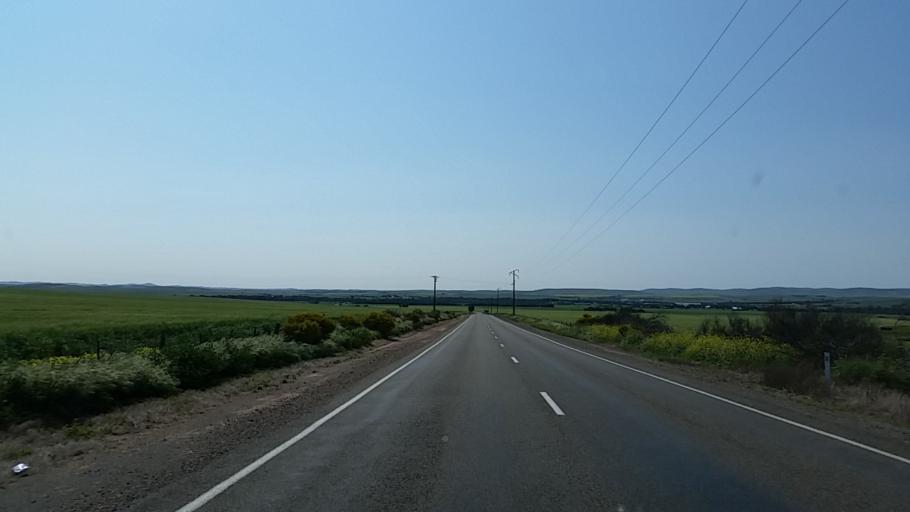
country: AU
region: South Australia
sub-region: Port Pirie City and Dists
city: Crystal Brook
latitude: -33.2770
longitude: 138.2999
